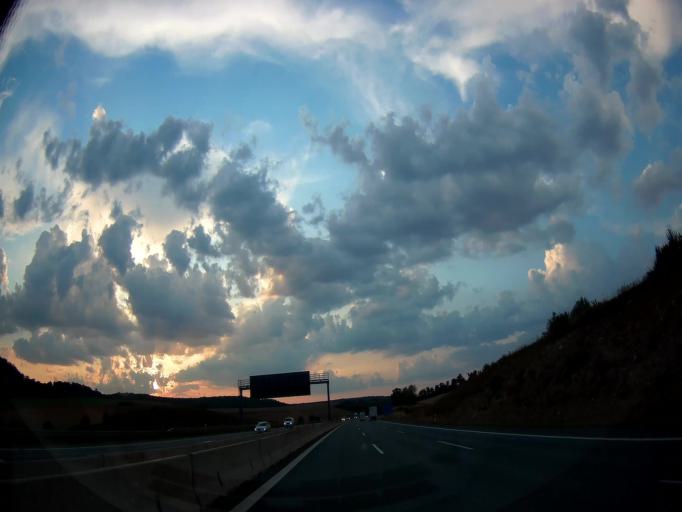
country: DE
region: Bavaria
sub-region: Regierungsbezirk Unterfranken
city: Waldbrunn
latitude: 49.7520
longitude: 9.7922
